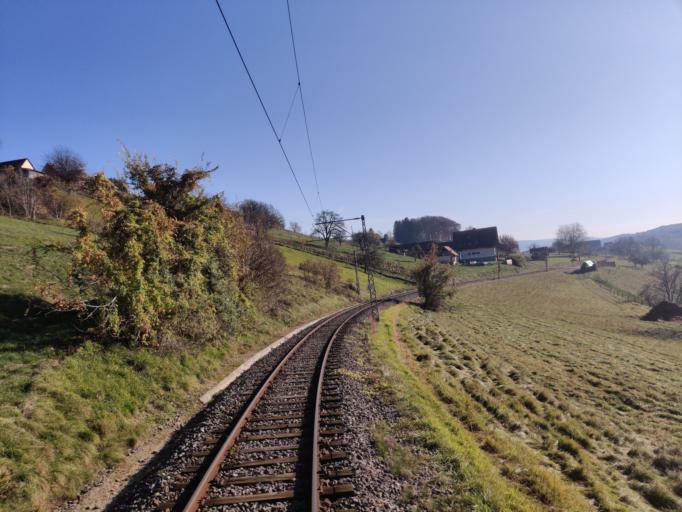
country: AT
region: Styria
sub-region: Politischer Bezirk Suedoststeiermark
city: Trautmannsdorf in Oststeiermark
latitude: 46.8854
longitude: 15.8820
